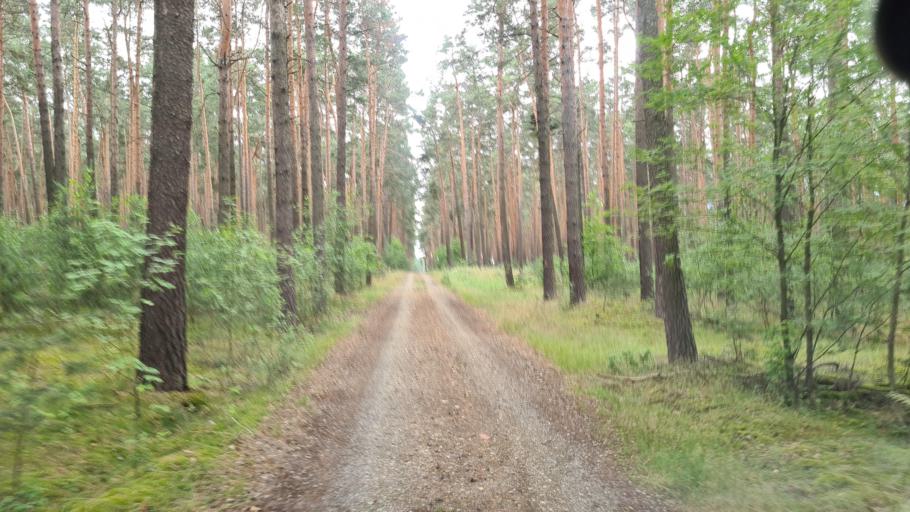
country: DE
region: Brandenburg
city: Bronkow
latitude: 51.6921
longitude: 13.8787
